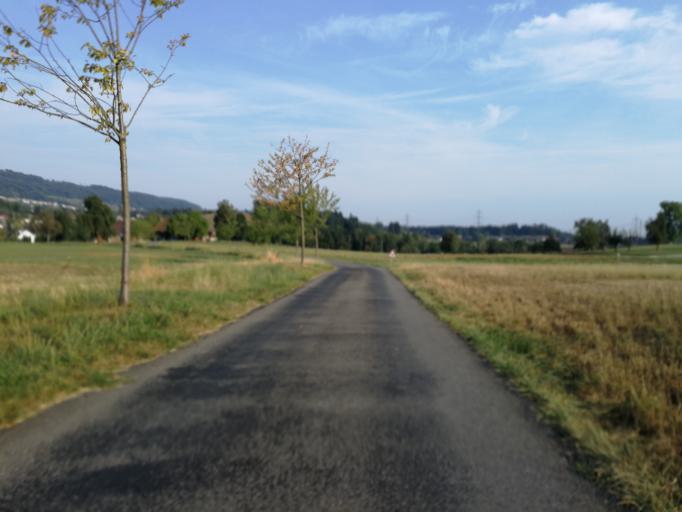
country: CH
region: Zurich
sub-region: Bezirk Uster
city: Esslingen
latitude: 47.2875
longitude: 8.7197
